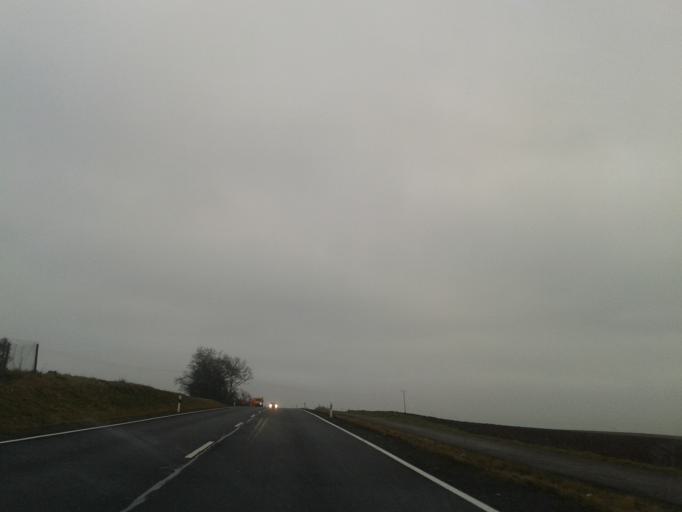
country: DE
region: Bavaria
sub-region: Regierungsbezirk Unterfranken
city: Pfarrweisach
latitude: 50.1956
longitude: 10.7703
